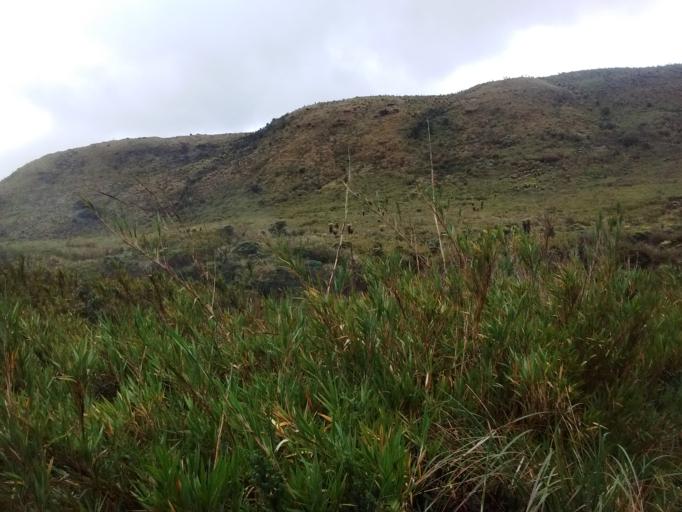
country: CO
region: Cauca
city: Totoro
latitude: 2.3576
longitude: -76.3171
